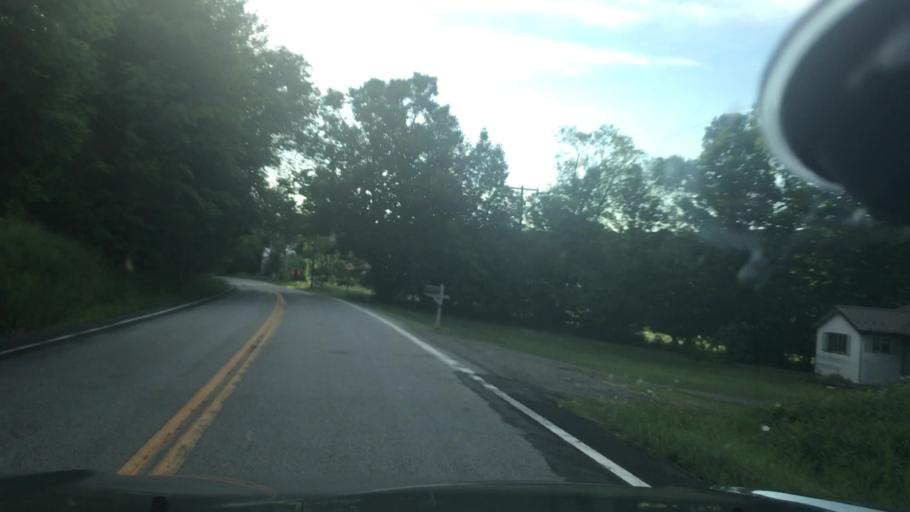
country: US
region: New York
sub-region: Otsego County
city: Unadilla
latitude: 42.3340
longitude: -75.2367
